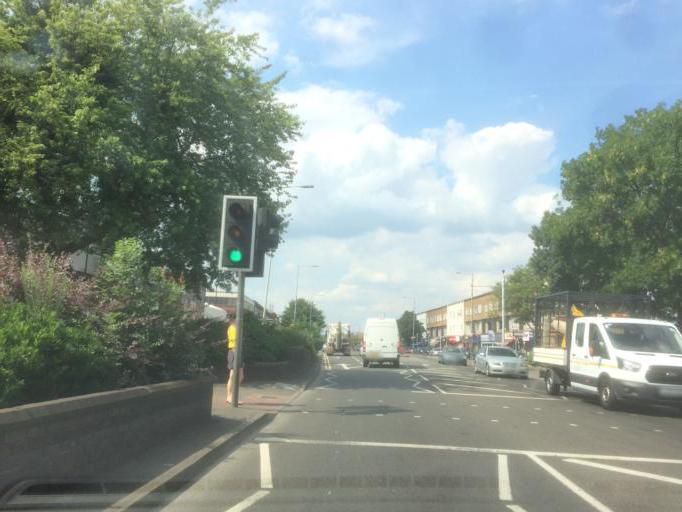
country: GB
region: England
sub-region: Buckinghamshire
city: Farnham Royal
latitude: 51.5234
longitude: -0.6153
